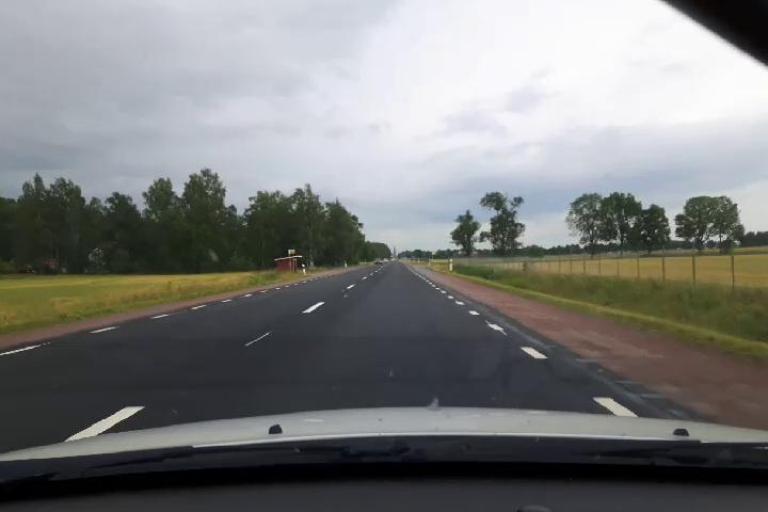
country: SE
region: Uppsala
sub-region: Uppsala Kommun
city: Gamla Uppsala
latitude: 59.8891
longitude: 17.6177
